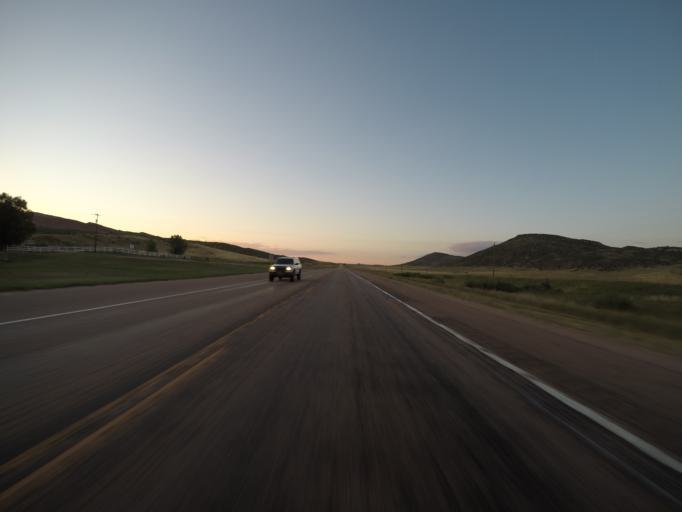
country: US
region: Colorado
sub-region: Larimer County
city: Laporte
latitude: 40.7301
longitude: -105.1714
